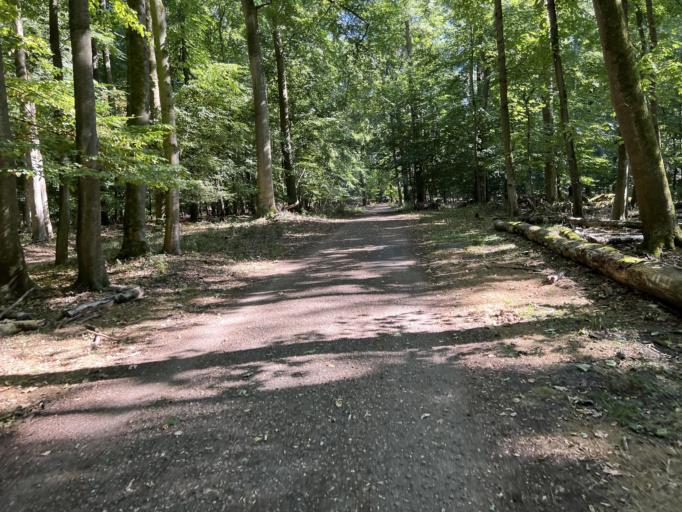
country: DE
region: Hesse
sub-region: Regierungsbezirk Darmstadt
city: Neu Isenburg
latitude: 50.0652
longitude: 8.6962
